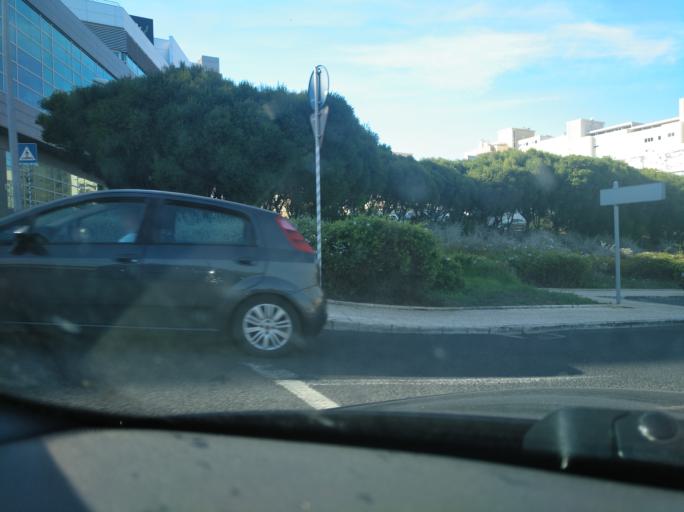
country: PT
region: Lisbon
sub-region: Oeiras
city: Linda-a-Velha
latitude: 38.7184
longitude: -9.2280
